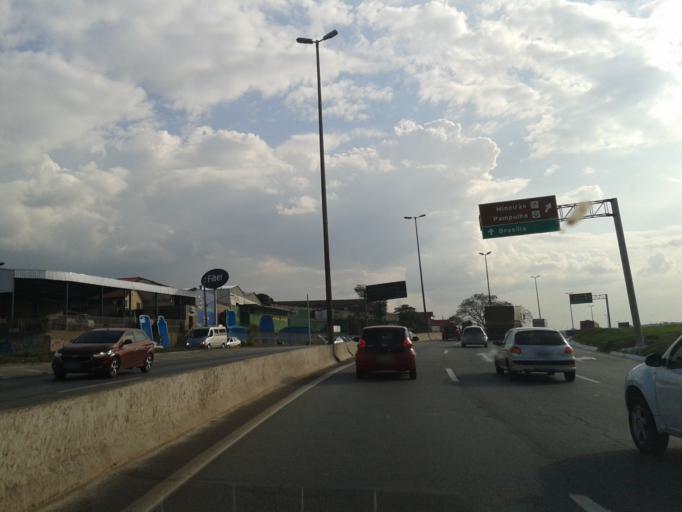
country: BR
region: Minas Gerais
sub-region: Belo Horizonte
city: Belo Horizonte
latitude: -19.8802
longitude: -43.9538
